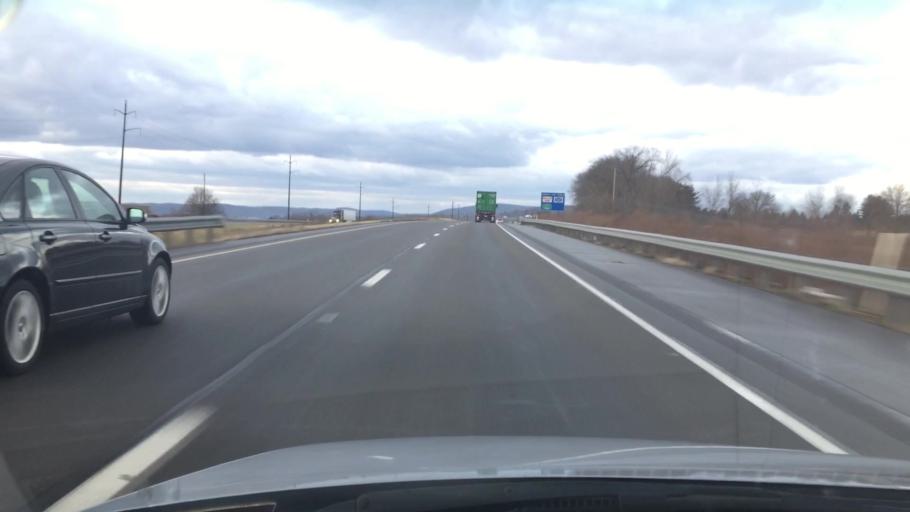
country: US
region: Pennsylvania
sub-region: Columbia County
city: Almedia
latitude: 41.0283
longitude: -76.3966
